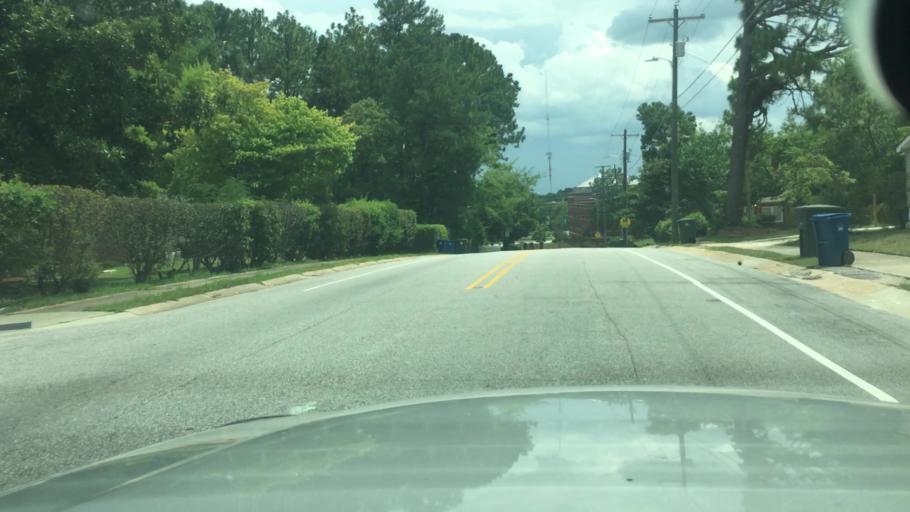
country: US
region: North Carolina
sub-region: Cumberland County
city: Fayetteville
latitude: 35.0796
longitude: -78.8940
